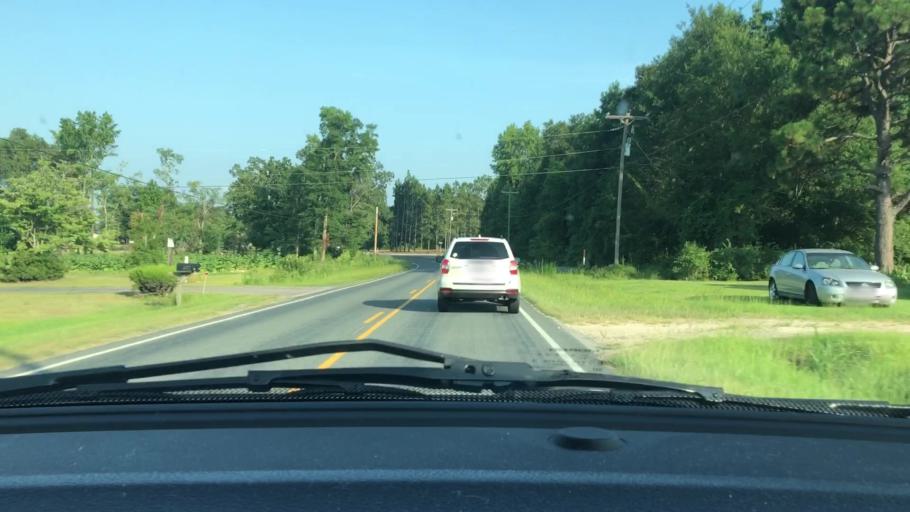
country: US
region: North Carolina
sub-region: Lee County
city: Broadway
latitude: 35.3490
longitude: -79.0708
